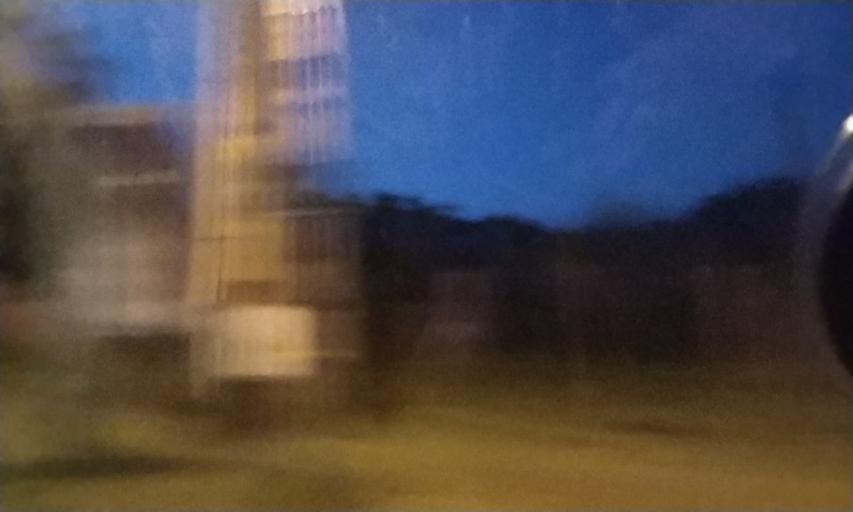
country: PT
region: Setubal
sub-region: Palmela
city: Palmela
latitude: 38.5437
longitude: -8.9106
